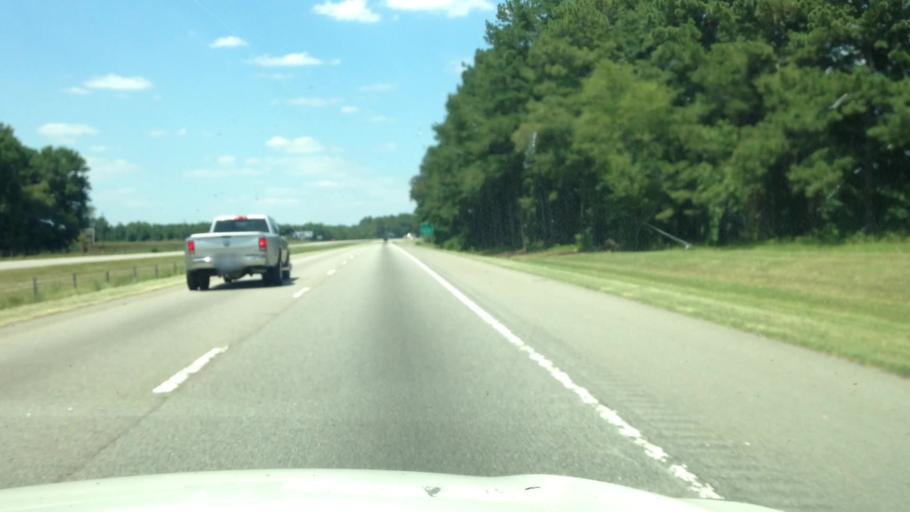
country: US
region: North Carolina
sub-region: Robeson County
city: Saint Pauls
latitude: 34.7869
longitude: -78.9946
